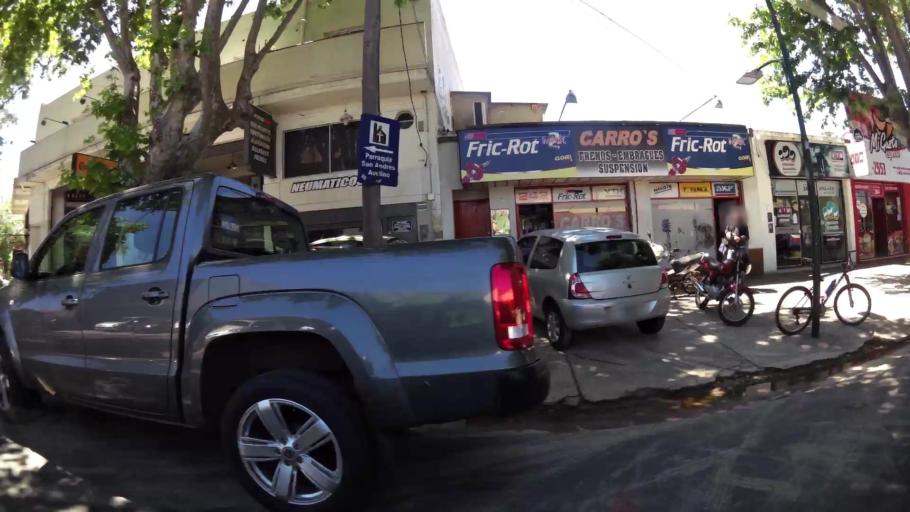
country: AR
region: Buenos Aires
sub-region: Partido de San Isidro
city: San Isidro
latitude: -34.5112
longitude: -58.5405
